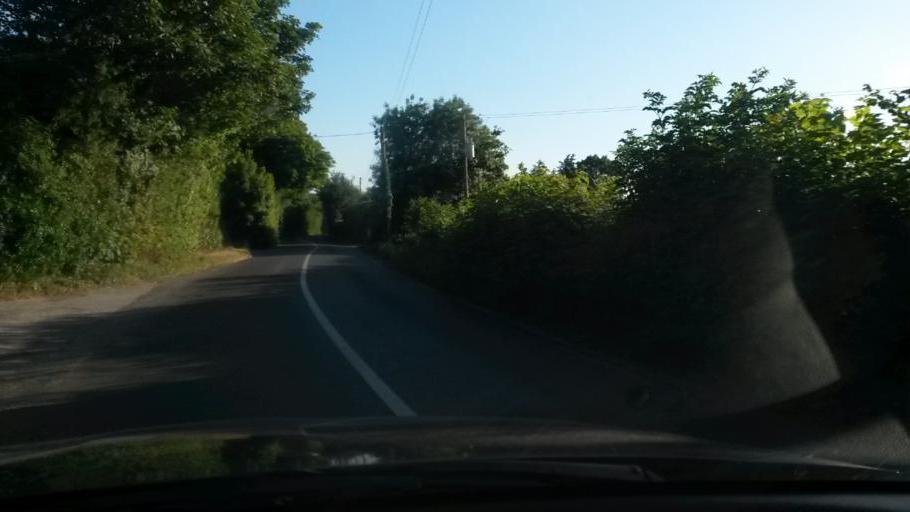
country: IE
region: Leinster
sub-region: Fingal County
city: Blanchardstown
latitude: 53.4346
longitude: -6.3593
